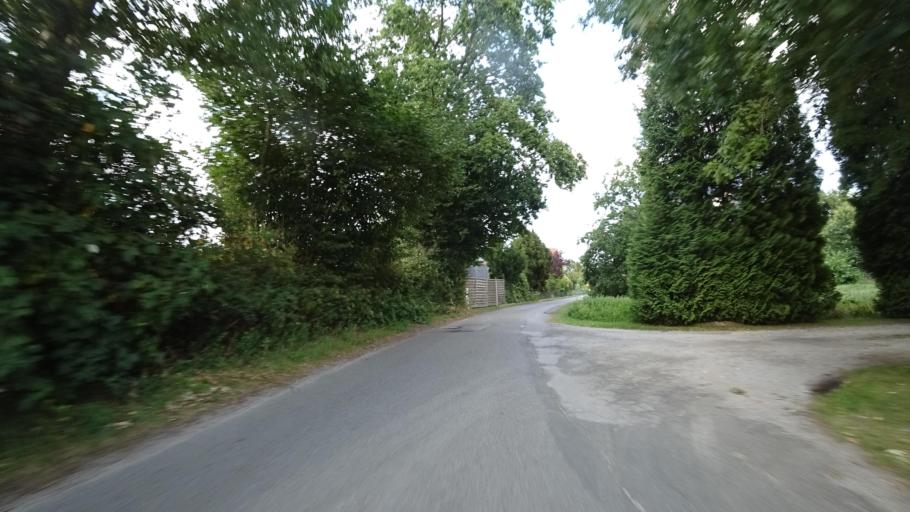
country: DE
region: North Rhine-Westphalia
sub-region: Regierungsbezirk Detmold
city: Steinhagen
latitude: 51.9541
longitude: 8.4613
